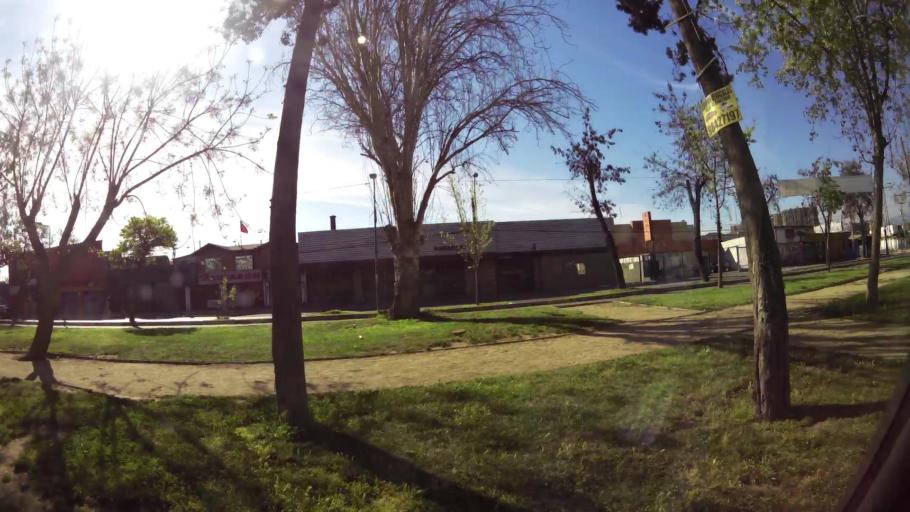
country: CL
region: Santiago Metropolitan
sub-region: Provincia de Santiago
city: Lo Prado
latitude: -33.4649
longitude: -70.7057
